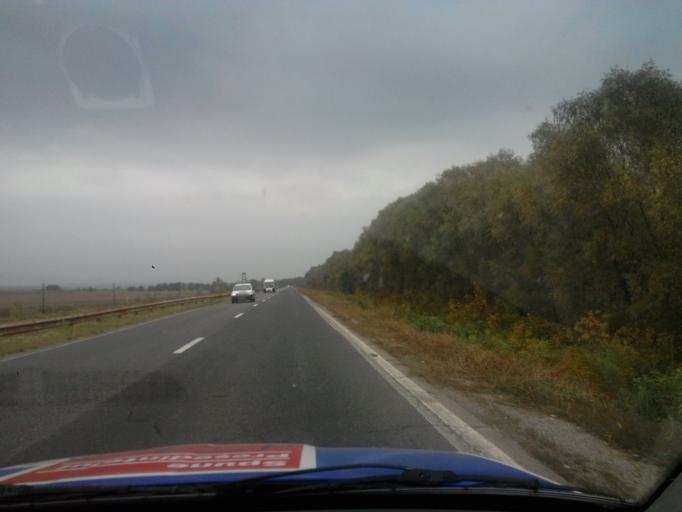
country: RO
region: Braila
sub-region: Municipiul Braila
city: Braila
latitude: 45.3332
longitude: 28.0017
